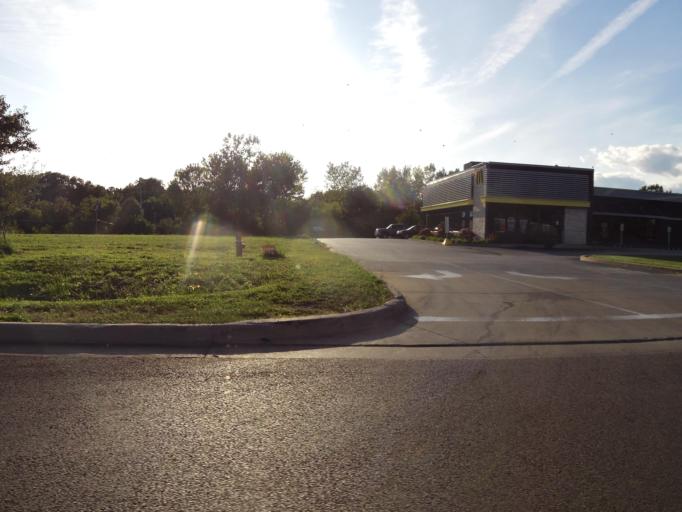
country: US
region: Indiana
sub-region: Tippecanoe County
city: Battle Ground
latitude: 40.5034
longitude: -86.8686
